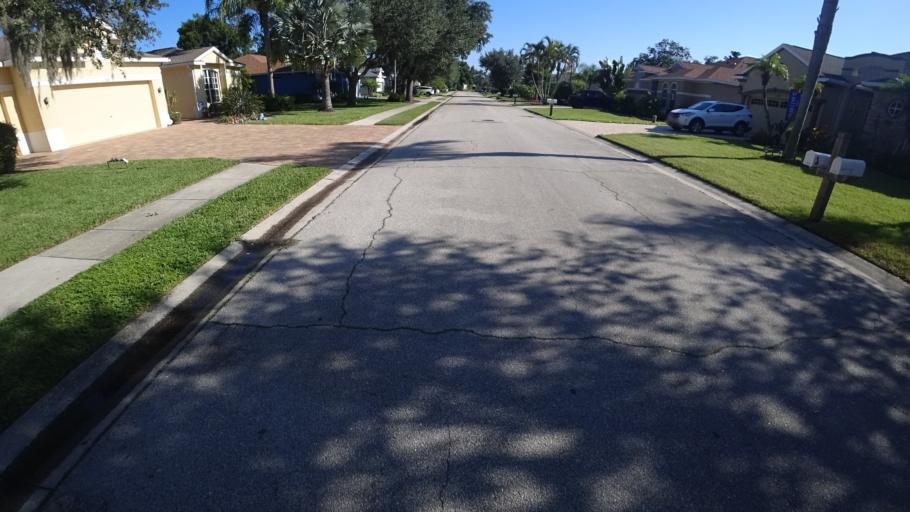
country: US
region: Florida
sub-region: Manatee County
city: Ellenton
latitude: 27.5031
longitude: -82.5144
